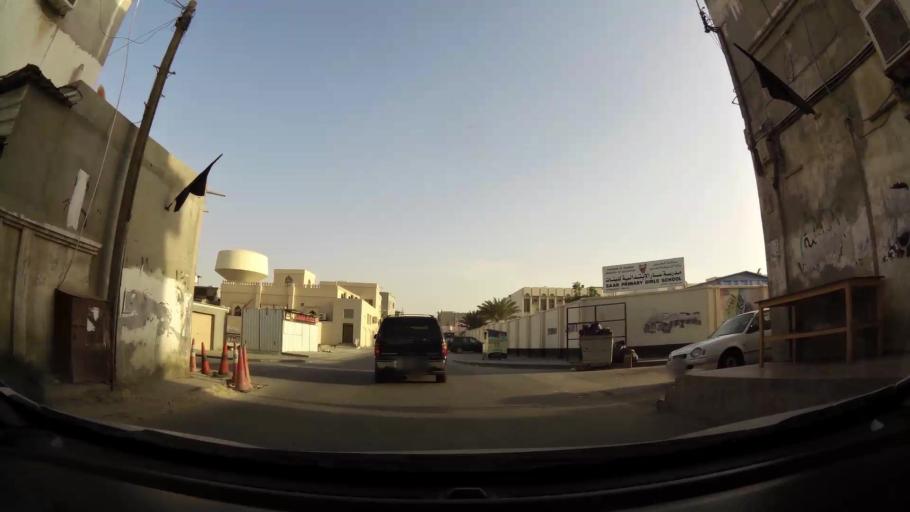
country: BH
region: Northern
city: Madinat `Isa
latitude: 26.1932
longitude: 50.4870
